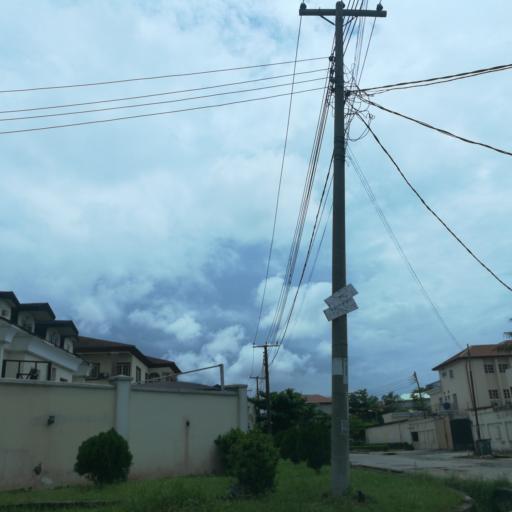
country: NG
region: Lagos
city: Ikoyi
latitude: 6.4440
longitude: 3.4615
